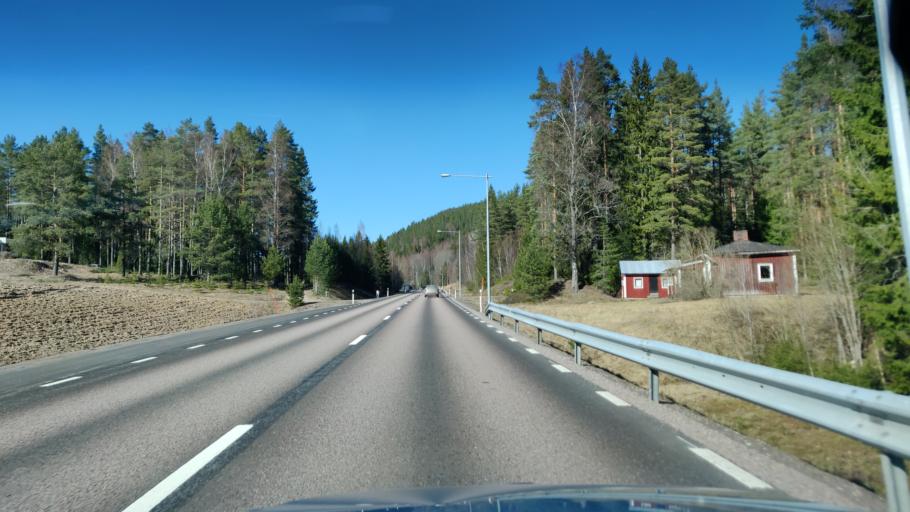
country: SE
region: Vaermland
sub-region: Hagfors Kommun
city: Hagfors
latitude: 59.9355
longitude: 13.6770
